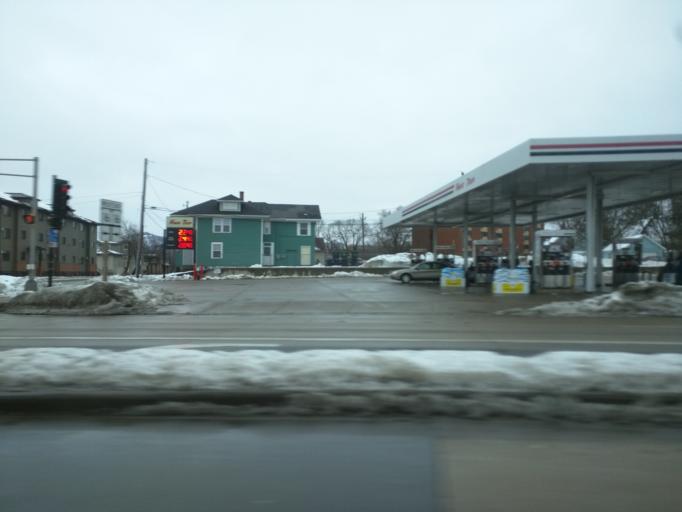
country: US
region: Wisconsin
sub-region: La Crosse County
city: La Crosse
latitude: 43.8172
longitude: -91.2391
